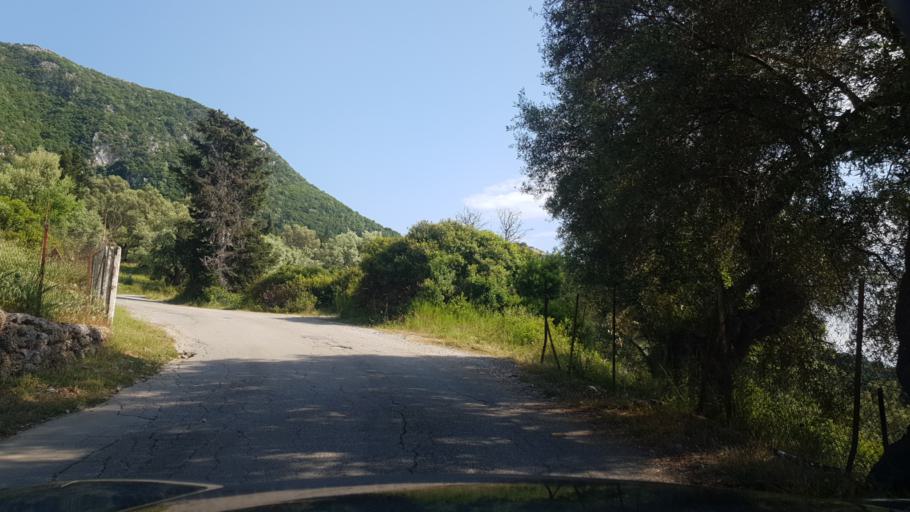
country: GR
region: Ionian Islands
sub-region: Lefkada
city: Nidri
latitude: 38.6464
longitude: 20.7048
